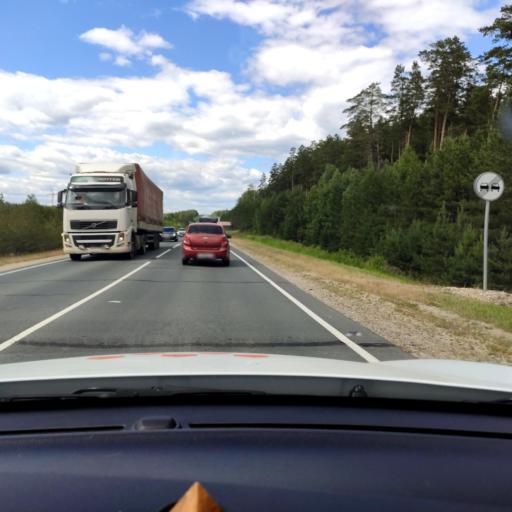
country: RU
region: Mariy-El
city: Volzhsk
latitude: 55.8950
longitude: 48.3947
